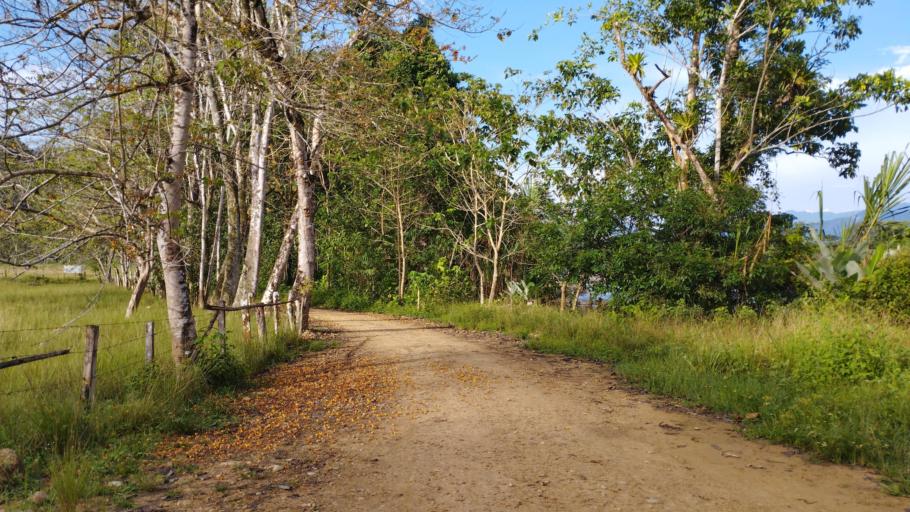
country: CO
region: Boyaca
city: San Luis de Gaceno
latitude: 4.8179
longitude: -73.1632
